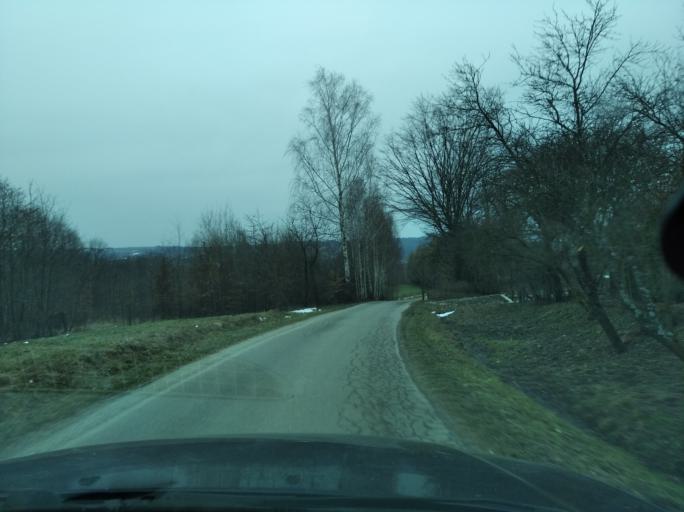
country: PL
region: Subcarpathian Voivodeship
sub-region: Powiat rzeszowski
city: Chmielnik
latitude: 49.9885
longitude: 22.1355
